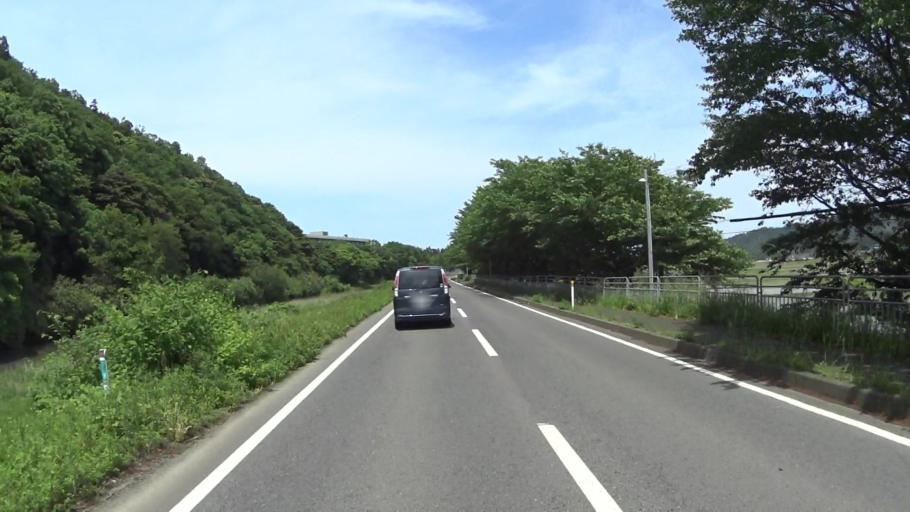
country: JP
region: Fukui
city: Obama
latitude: 35.4589
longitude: 135.6075
